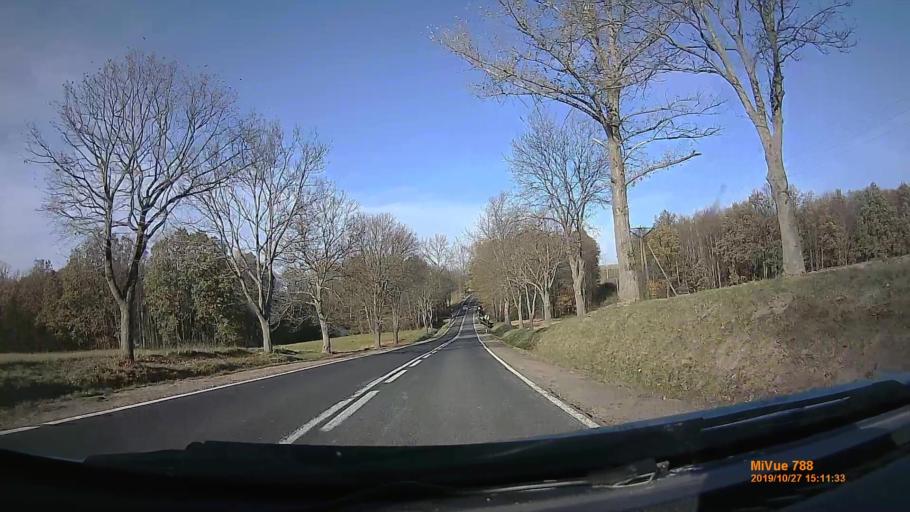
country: PL
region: Lower Silesian Voivodeship
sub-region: Powiat klodzki
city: Miedzylesie
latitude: 50.1989
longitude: 16.6720
